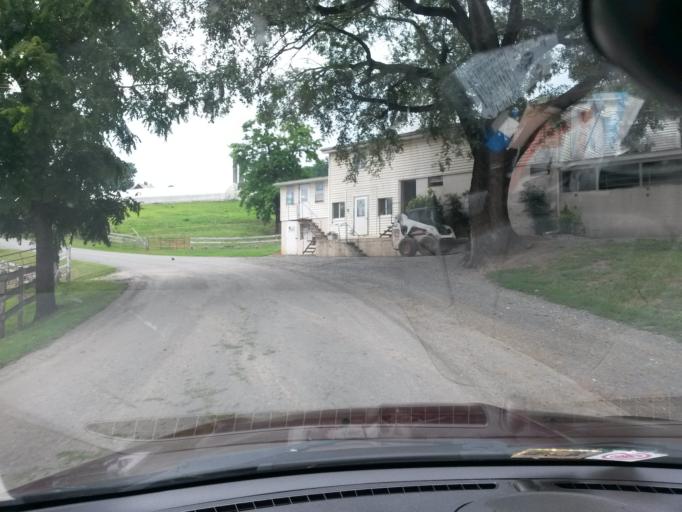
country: US
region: Virginia
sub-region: Rockingham County
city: Dayton
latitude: 38.4426
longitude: -78.9516
